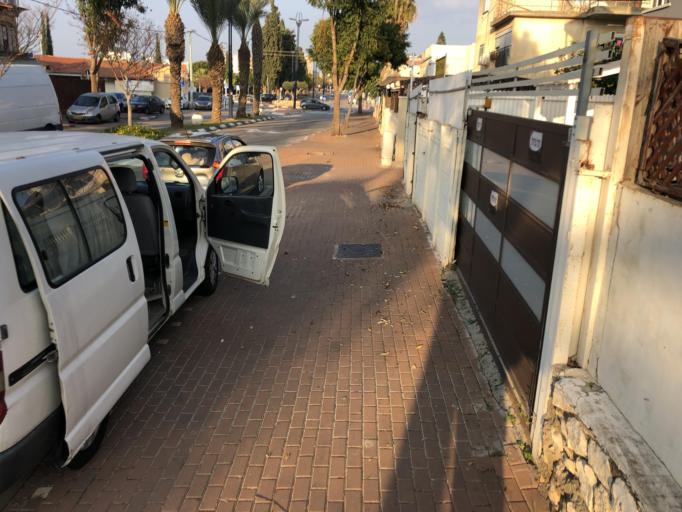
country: IL
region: Northern District
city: `Akko
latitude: 32.9265
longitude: 35.0867
